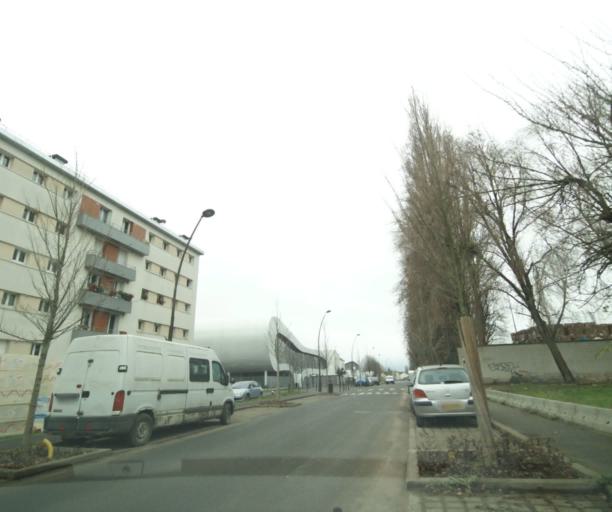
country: FR
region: Ile-de-France
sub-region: Departement du Val-de-Marne
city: Villeneuve-Saint-Georges
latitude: 48.7344
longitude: 2.4401
